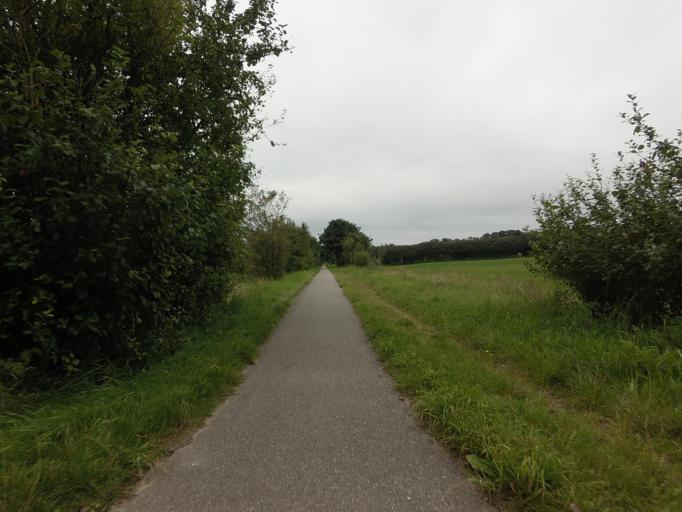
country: DK
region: Central Jutland
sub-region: Silkeborg Kommune
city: Virklund
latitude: 56.0790
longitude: 9.5260
